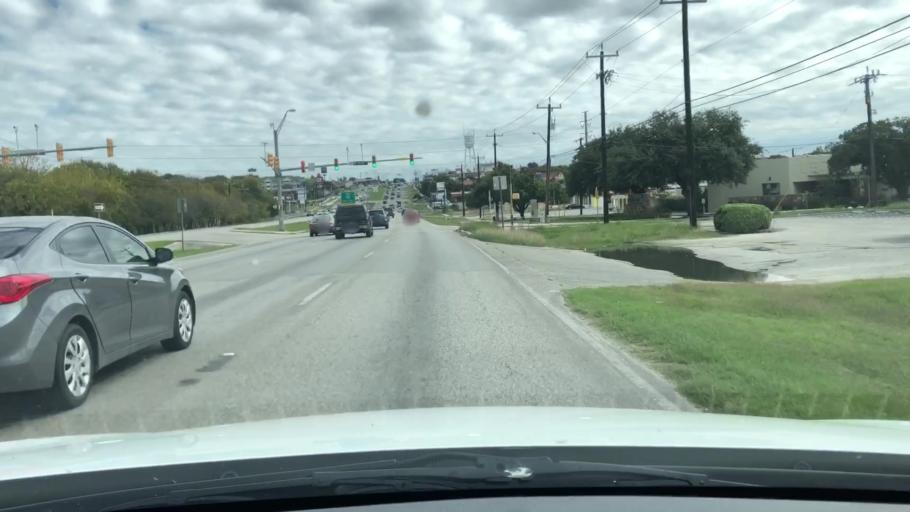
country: US
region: Texas
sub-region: Bexar County
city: Leon Valley
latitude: 29.4935
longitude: -98.6167
